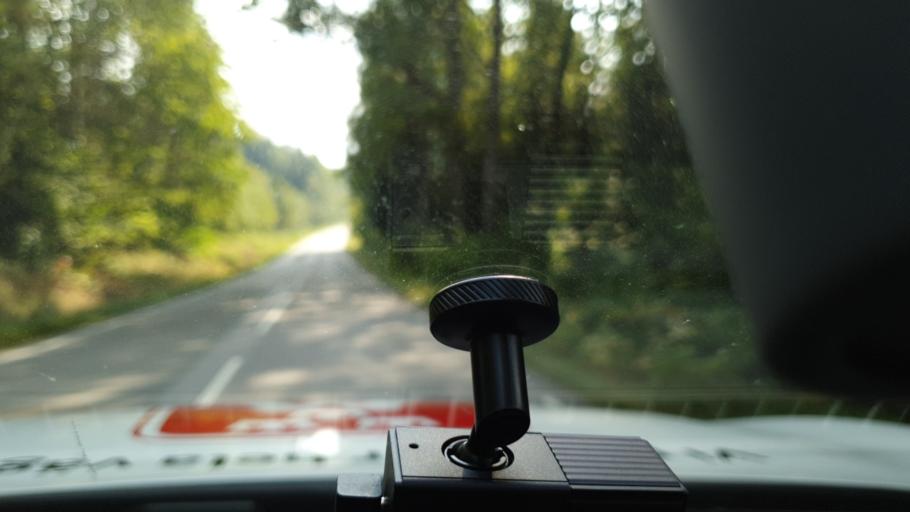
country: SE
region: Kalmar
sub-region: Vimmerby Kommun
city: Sodra Vi
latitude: 57.7229
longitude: 15.8363
